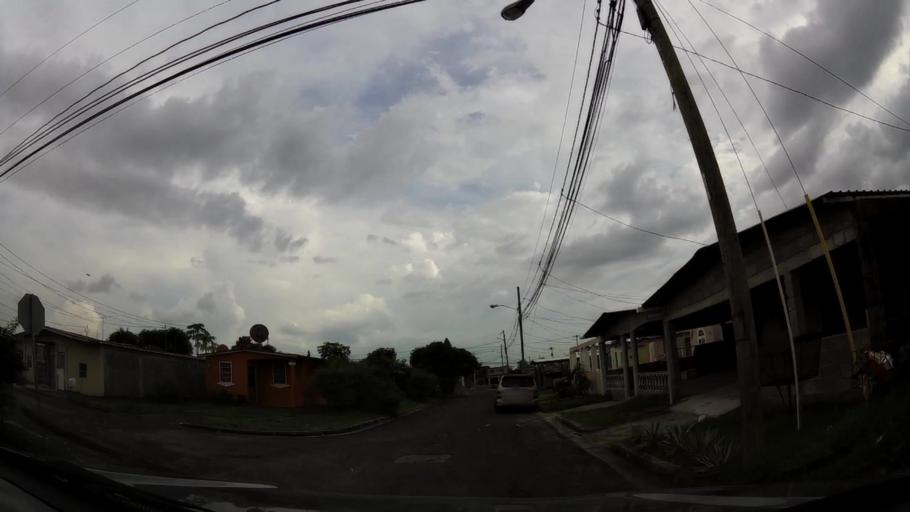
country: PA
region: Panama
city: Cabra Numero Uno
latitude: 9.0898
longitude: -79.3497
